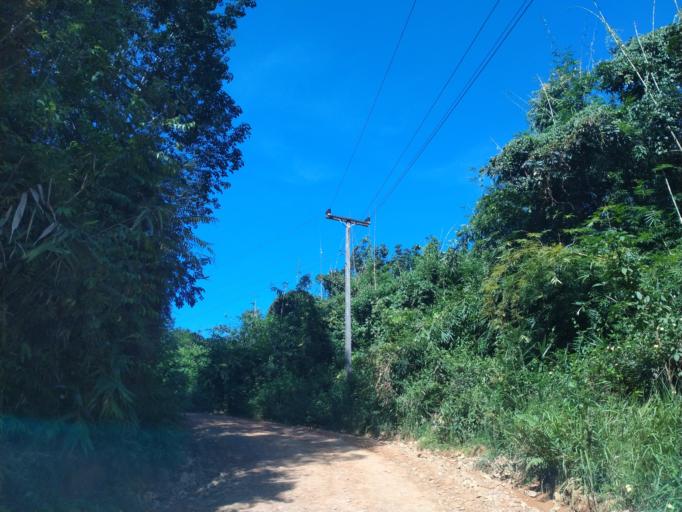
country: TH
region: Changwat Bueng Kan
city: Pak Khat
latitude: 18.6340
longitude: 103.0624
